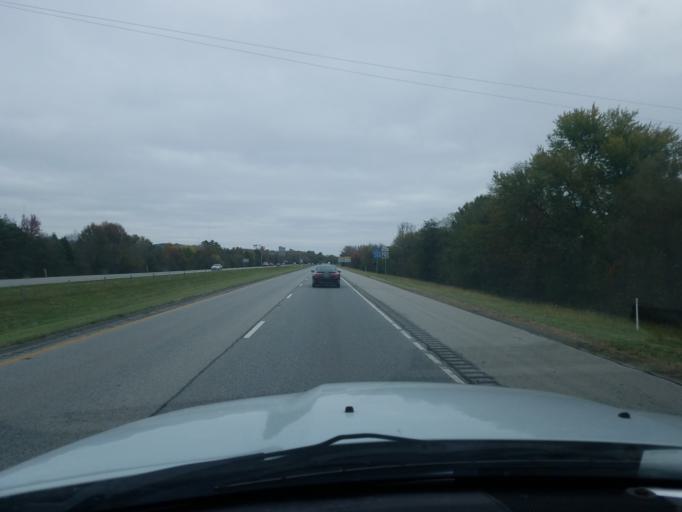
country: US
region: Indiana
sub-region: Floyd County
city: New Albany
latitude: 38.3171
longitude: -85.8418
